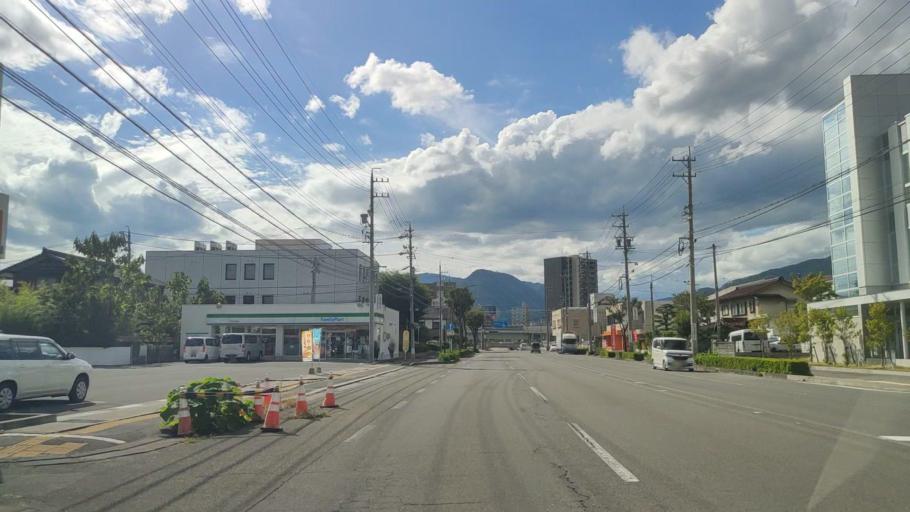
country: JP
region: Nagano
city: Nagano-shi
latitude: 36.6539
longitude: 138.2081
